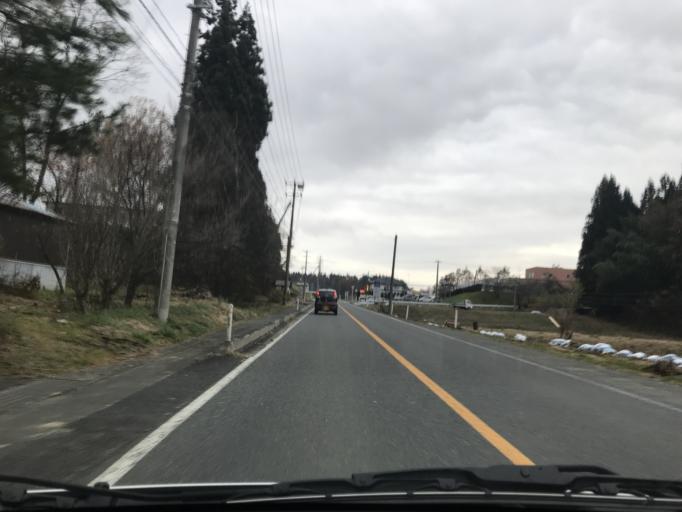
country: JP
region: Iwate
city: Ichinoseki
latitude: 39.0078
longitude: 141.3256
